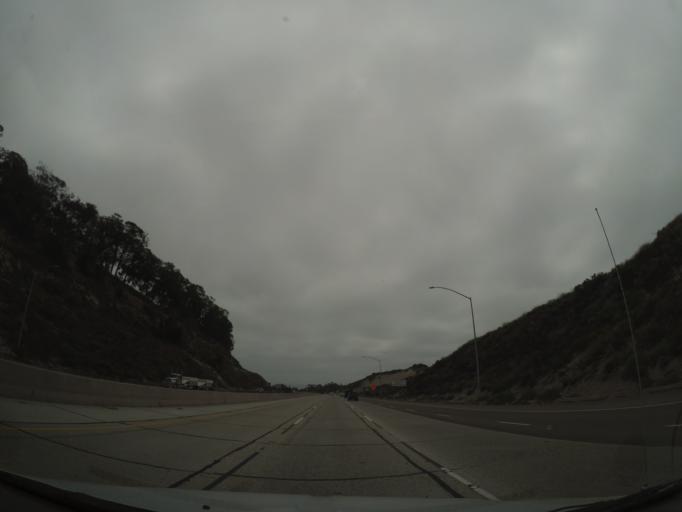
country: US
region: California
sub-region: Santa Barbara County
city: Carpinteria
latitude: 34.3816
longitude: -119.4828
